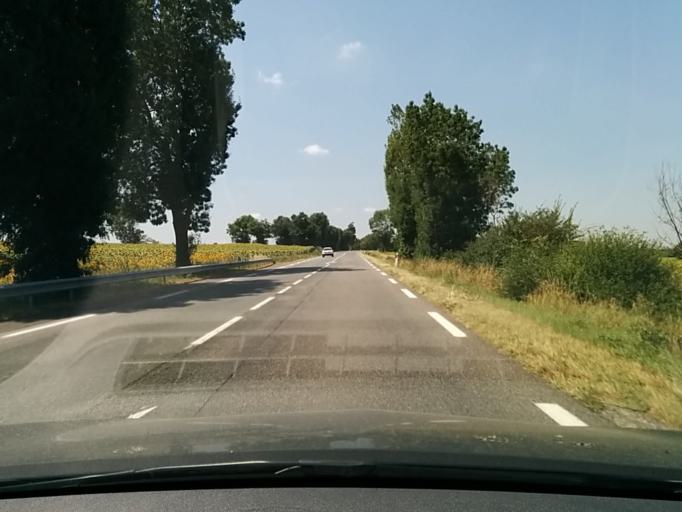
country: FR
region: Midi-Pyrenees
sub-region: Departement du Gers
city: Pujaudran
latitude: 43.6025
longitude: 1.0136
